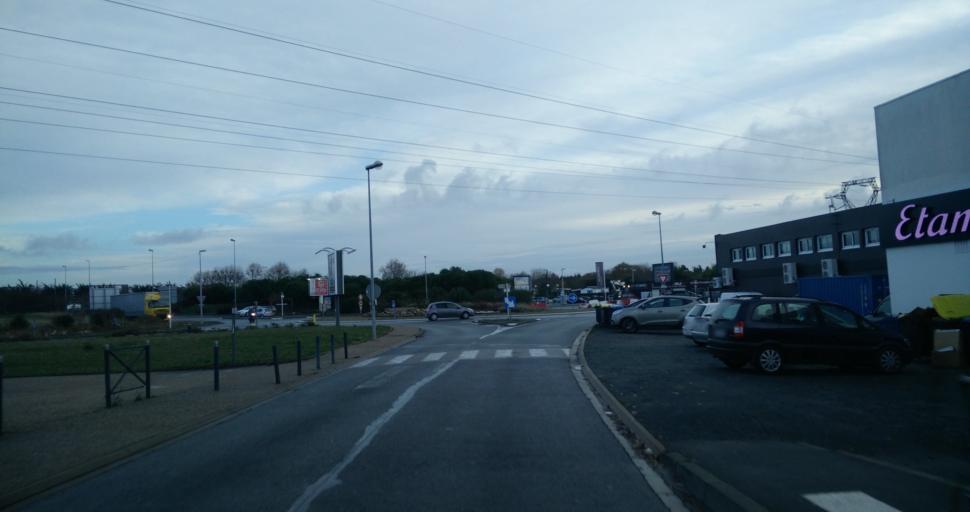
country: FR
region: Poitou-Charentes
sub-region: Departement de la Charente-Maritime
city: Puilboreau
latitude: 46.1771
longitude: -1.1171
